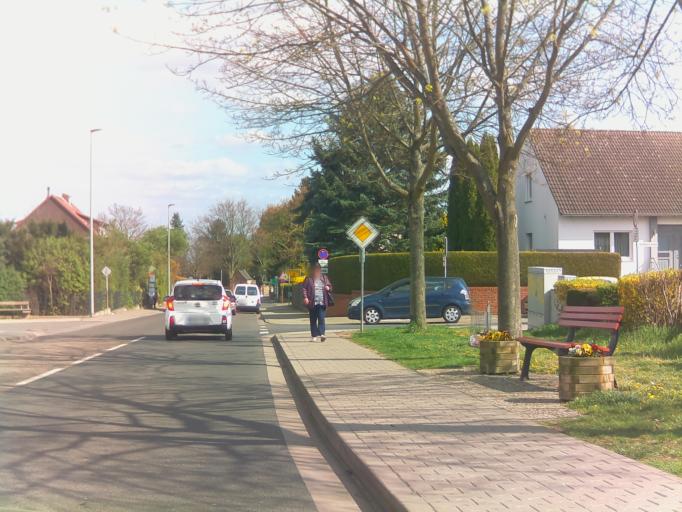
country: DE
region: Rheinland-Pfalz
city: Zornheim
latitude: 49.8901
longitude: 8.2216
